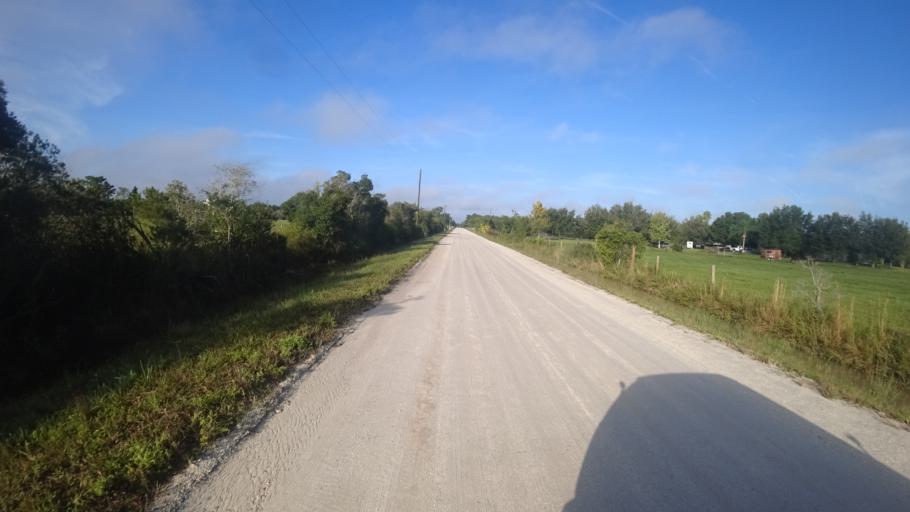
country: US
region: Florida
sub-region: Sarasota County
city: Fruitville
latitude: 27.4016
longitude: -82.2922
